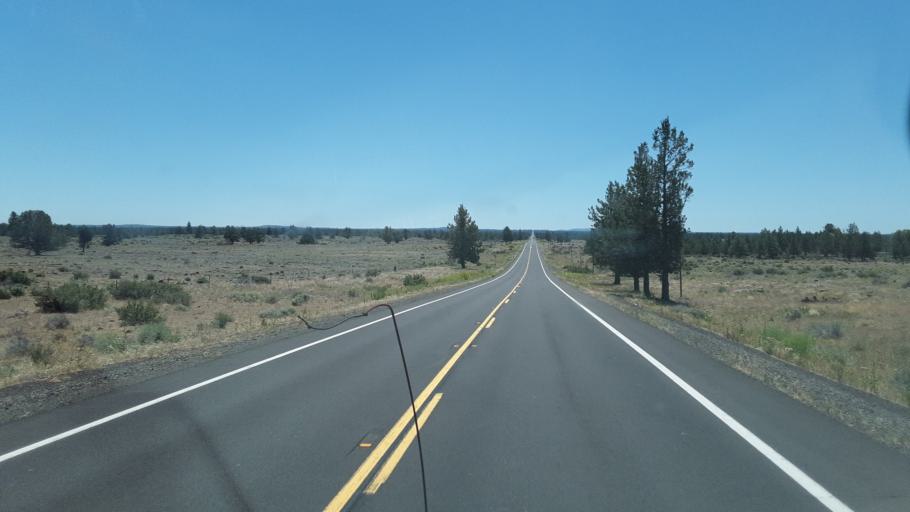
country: US
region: California
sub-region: Siskiyou County
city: Tulelake
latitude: 41.6829
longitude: -121.2669
